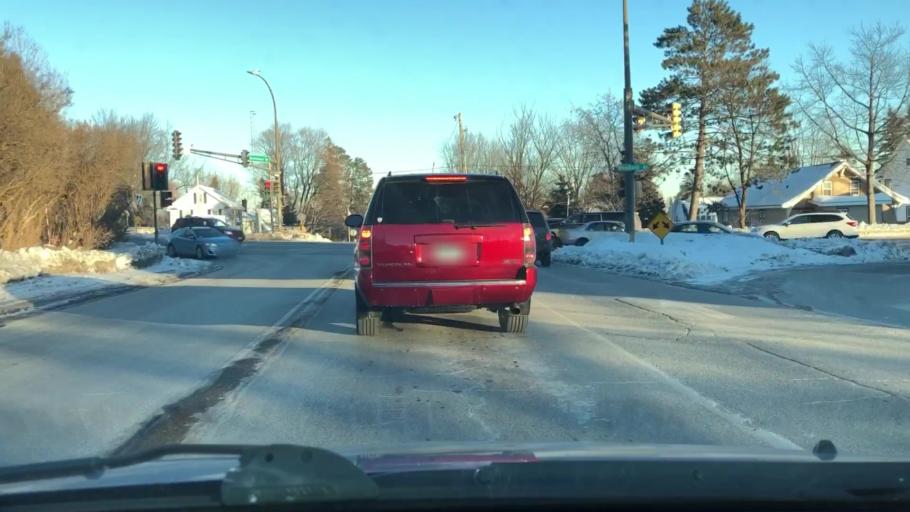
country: US
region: Minnesota
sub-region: Saint Louis County
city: Duluth
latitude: 46.8258
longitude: -92.0720
